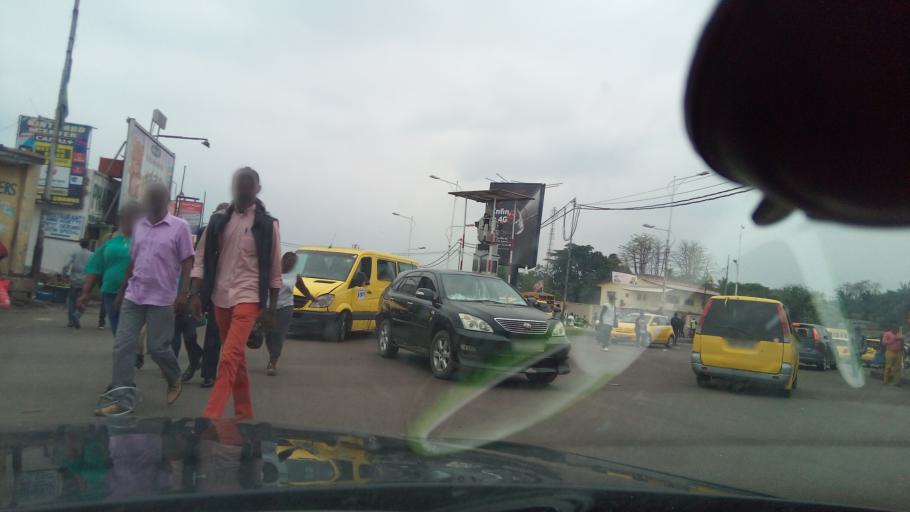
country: CD
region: Kinshasa
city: Kinshasa
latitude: -4.3343
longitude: 15.2581
